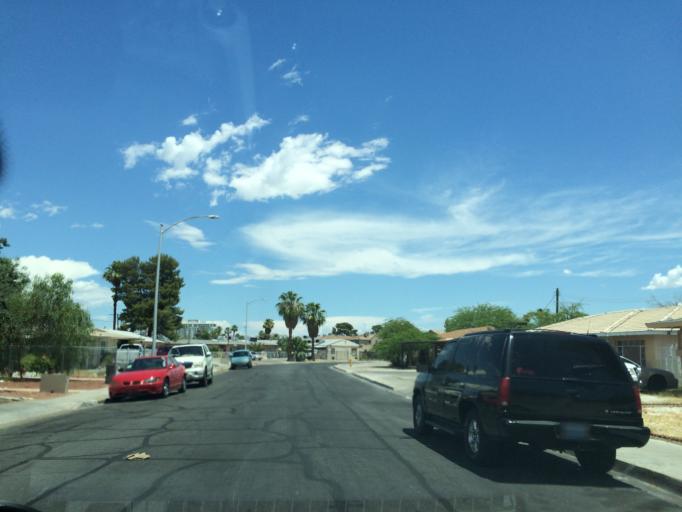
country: US
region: Nevada
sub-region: Clark County
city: Las Vegas
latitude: 36.1492
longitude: -115.1520
